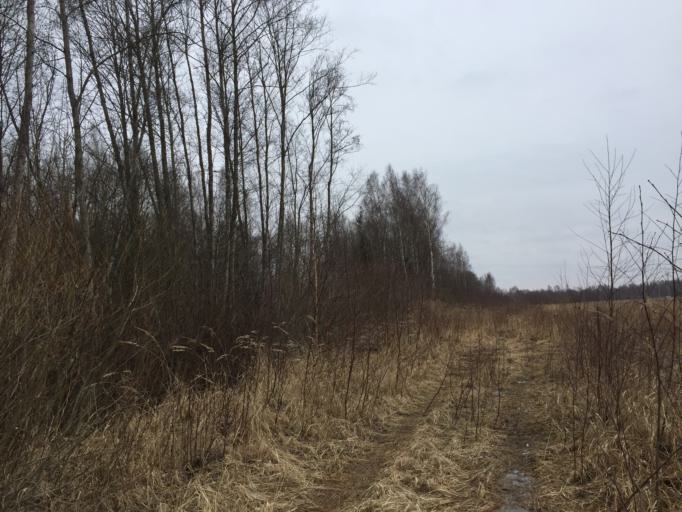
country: LV
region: Lielvarde
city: Lielvarde
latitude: 56.7643
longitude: 24.8195
